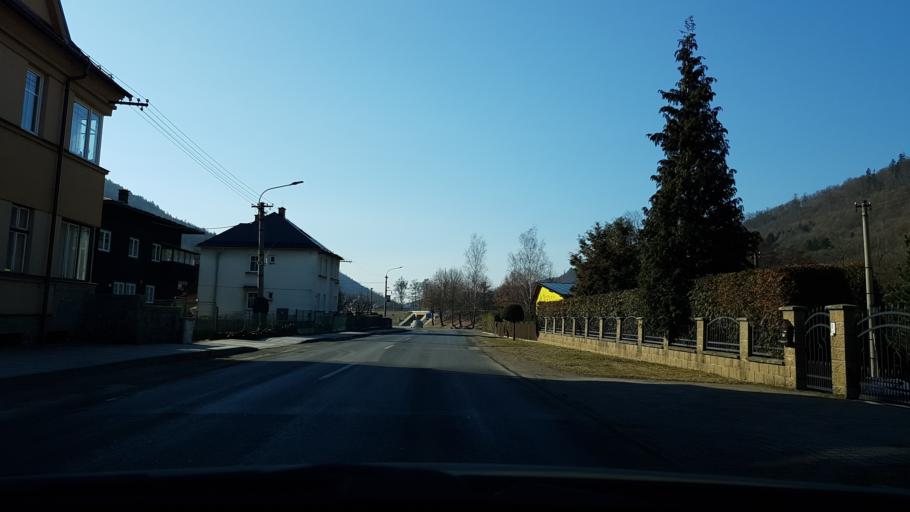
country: CZ
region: Olomoucky
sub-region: Okres Sumperk
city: Hanusovice
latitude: 50.0704
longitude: 16.9311
